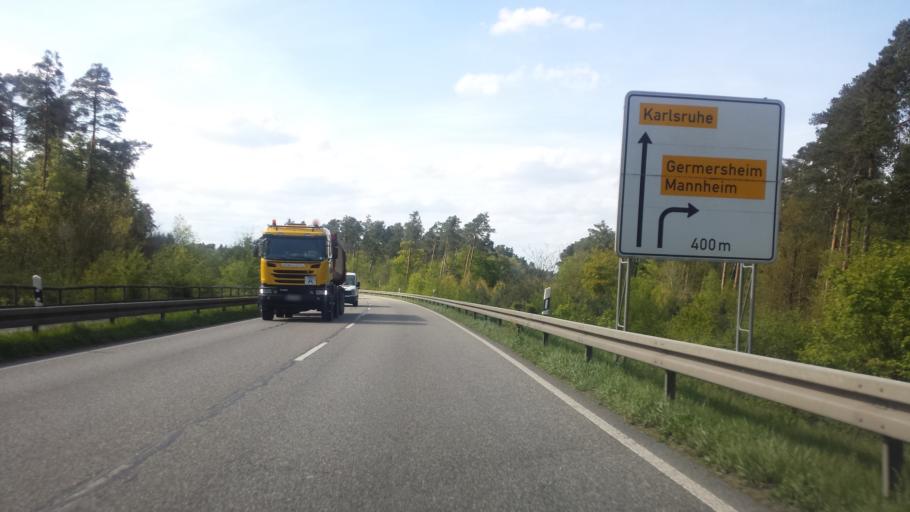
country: DE
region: Baden-Wuerttemberg
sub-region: Karlsruhe Region
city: Karlsdorf-Neuthard
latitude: 49.1526
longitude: 8.5147
